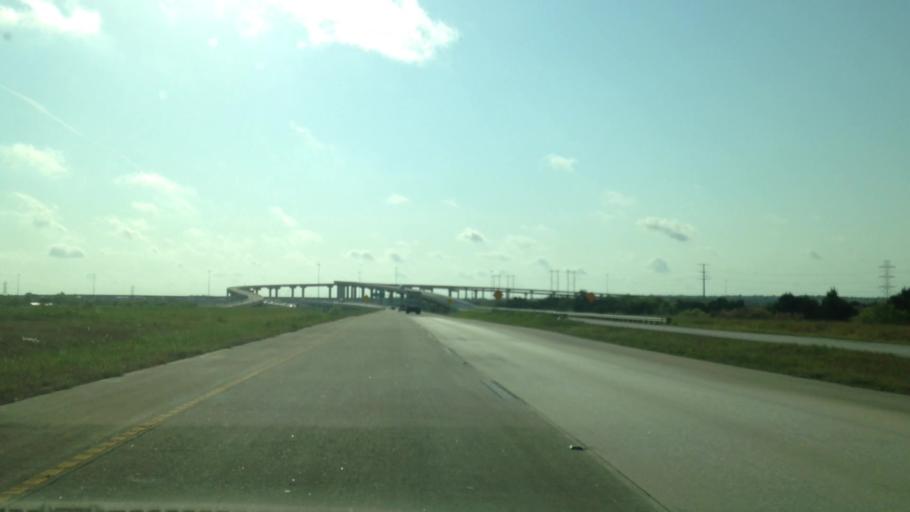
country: US
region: Texas
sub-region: Travis County
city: Onion Creek
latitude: 30.0815
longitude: -97.7062
